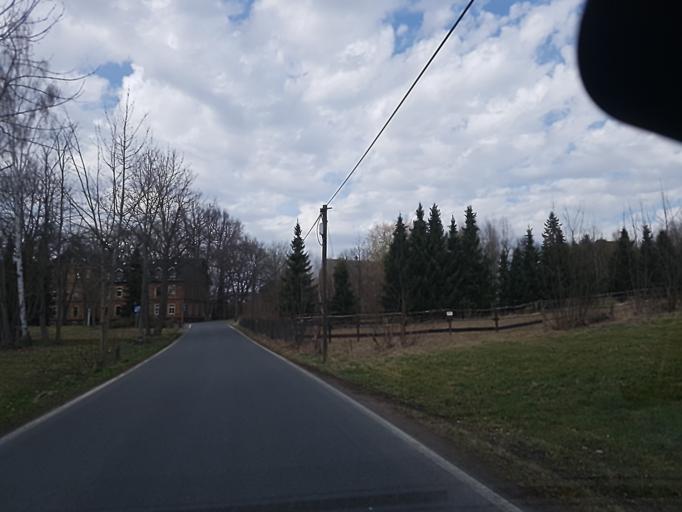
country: DE
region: Saxony
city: Grossweitzschen
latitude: 51.1423
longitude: 13.0358
